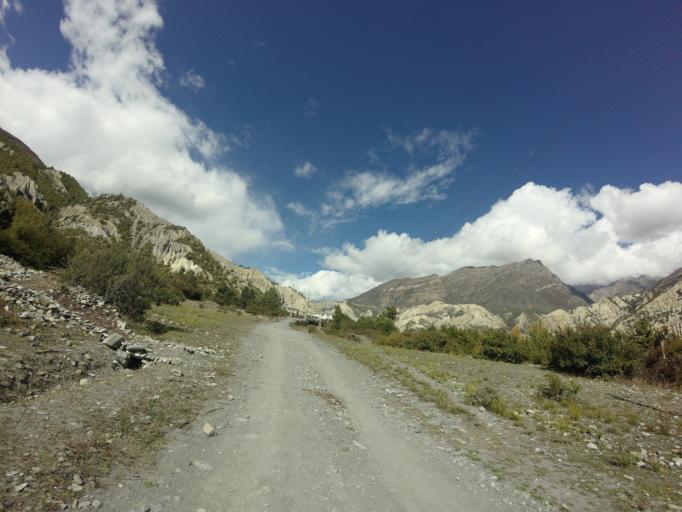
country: NP
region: Western Region
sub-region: Gandaki Zone
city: Nawal
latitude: 28.6369
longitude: 84.0930
